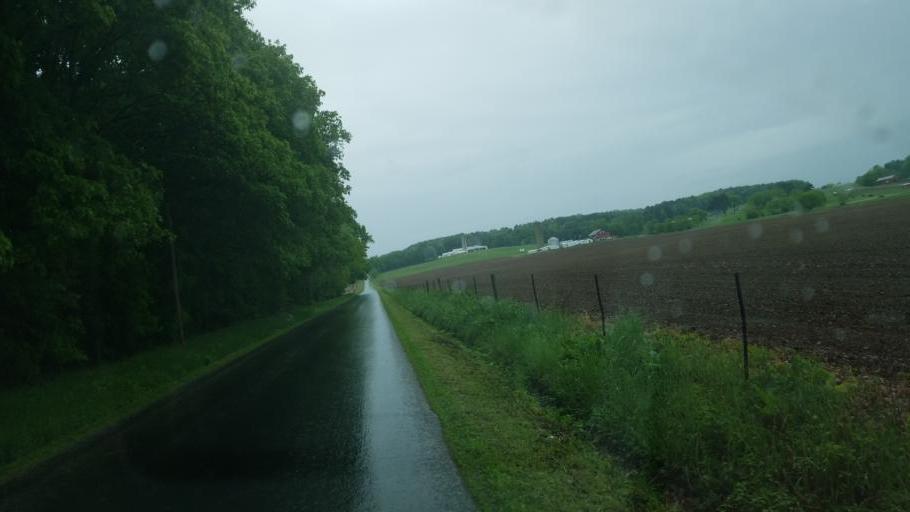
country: US
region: Ohio
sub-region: Wayne County
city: Apple Creek
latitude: 40.7618
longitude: -81.8536
